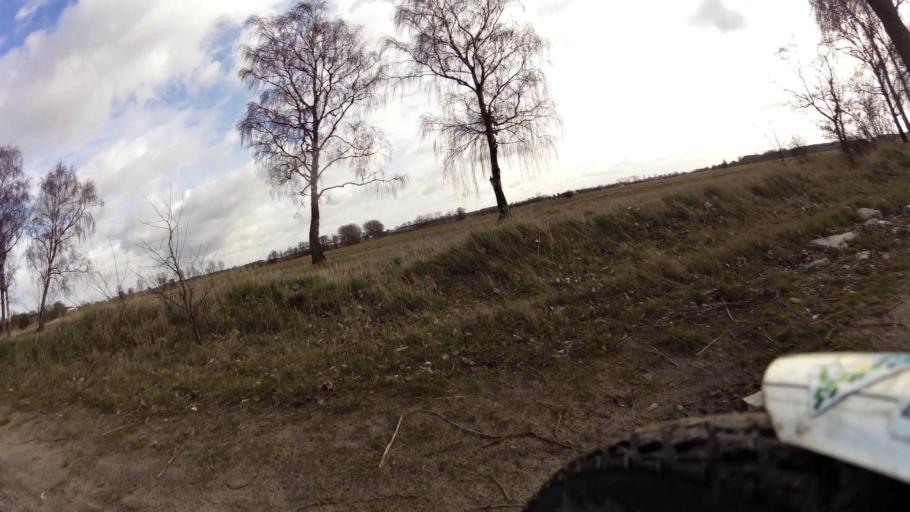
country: PL
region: West Pomeranian Voivodeship
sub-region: Powiat kamienski
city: Dziwnow
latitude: 54.0088
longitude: 14.8029
